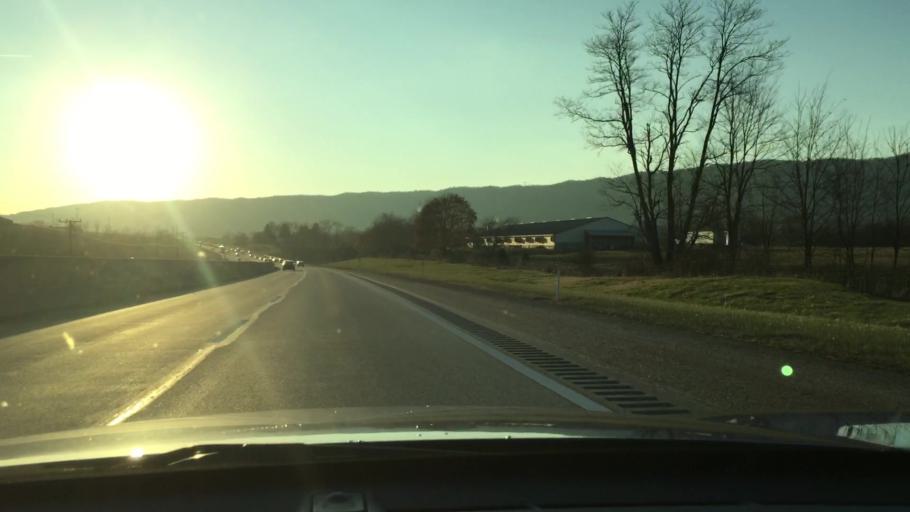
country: US
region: Pennsylvania
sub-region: Franklin County
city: Doylestown
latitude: 40.1210
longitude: -77.7726
